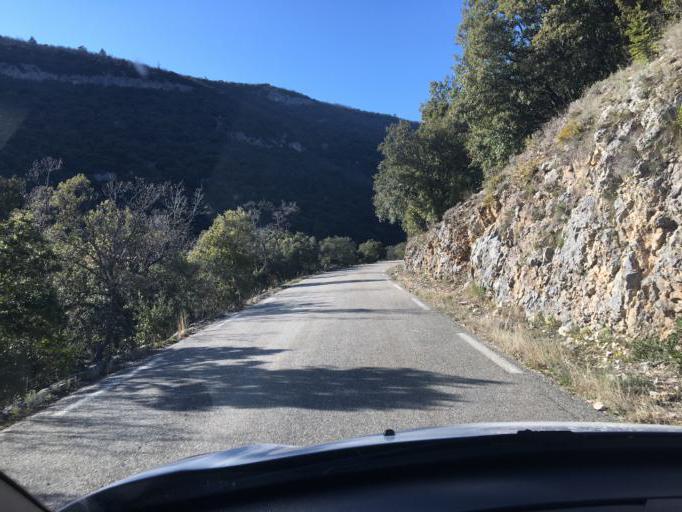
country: FR
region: Provence-Alpes-Cote d'Azur
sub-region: Departement du Vaucluse
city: Villes-sur-Auzon
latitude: 44.0669
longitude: 5.3077
